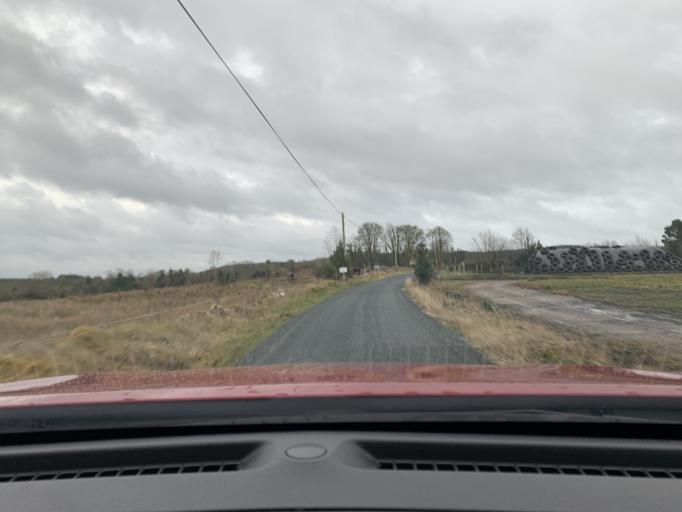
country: IE
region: Connaught
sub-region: Roscommon
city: Ballaghaderreen
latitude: 53.9689
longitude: -8.5197
